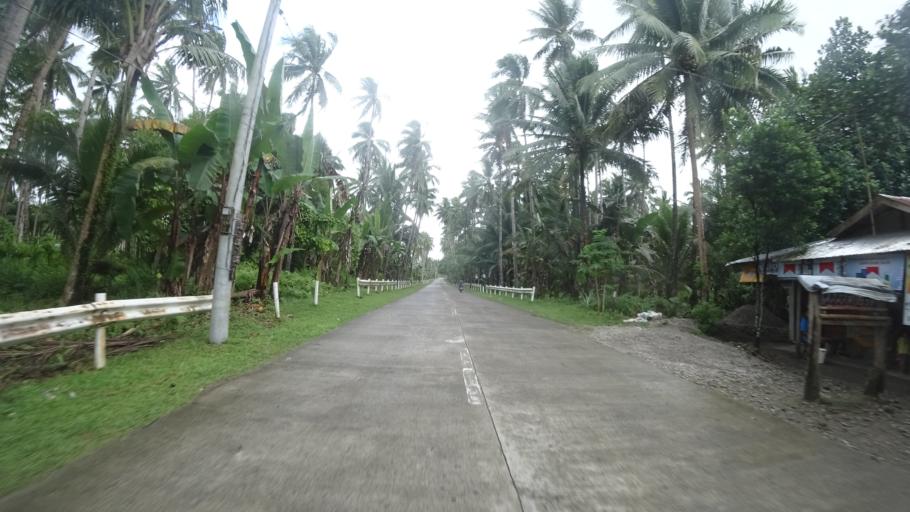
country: PH
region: Eastern Visayas
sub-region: Province of Leyte
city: Bugho
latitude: 10.8303
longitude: 124.9362
